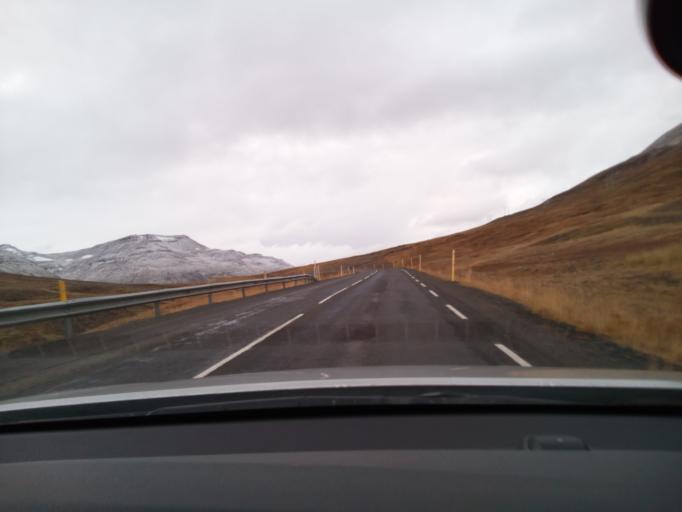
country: IS
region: Northeast
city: Dalvik
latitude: 65.4716
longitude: -18.6771
